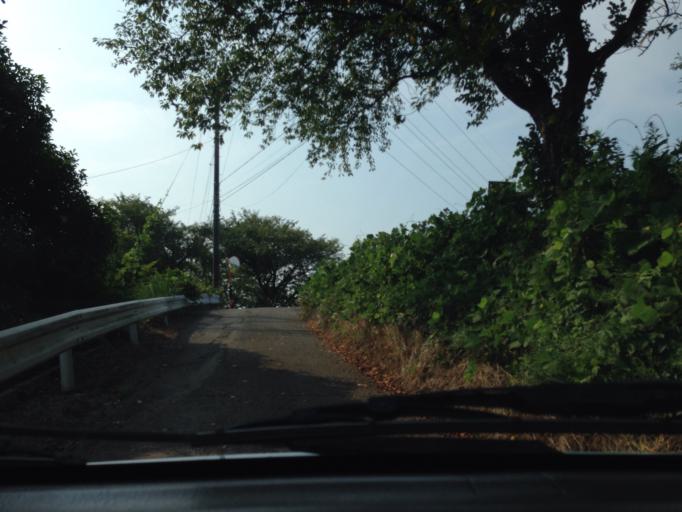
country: JP
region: Ibaraki
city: Ami
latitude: 36.0538
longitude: 140.2140
